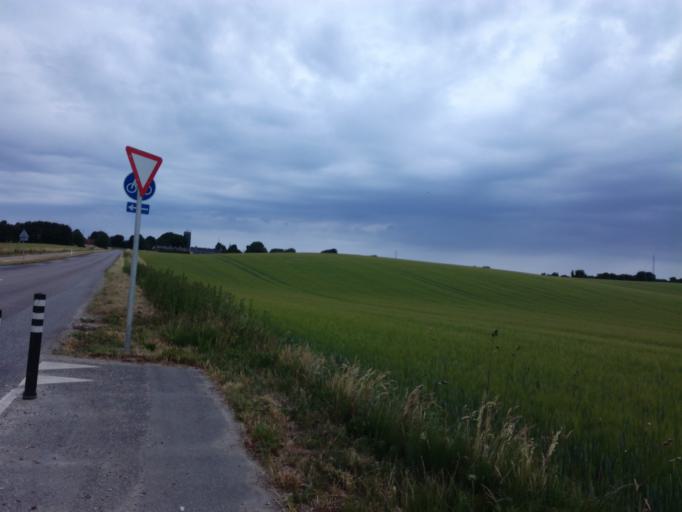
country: DK
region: South Denmark
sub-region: Vejle Kommune
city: Borkop
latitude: 55.6546
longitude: 9.6409
